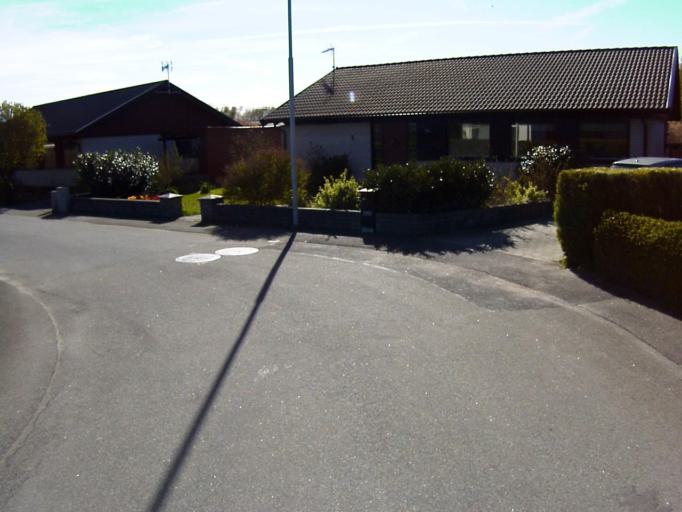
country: SE
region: Skane
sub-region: Kristianstads Kommun
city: Kristianstad
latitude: 56.0133
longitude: 14.1467
